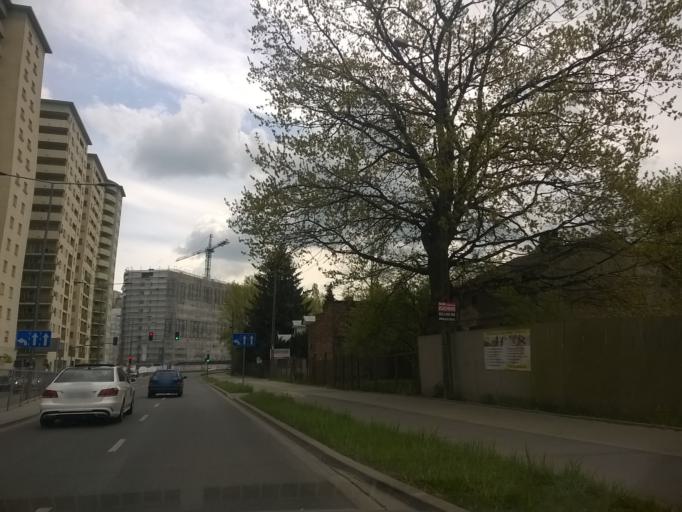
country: PL
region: Masovian Voivodeship
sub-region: Warszawa
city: Mokotow
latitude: 52.1802
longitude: 21.0265
